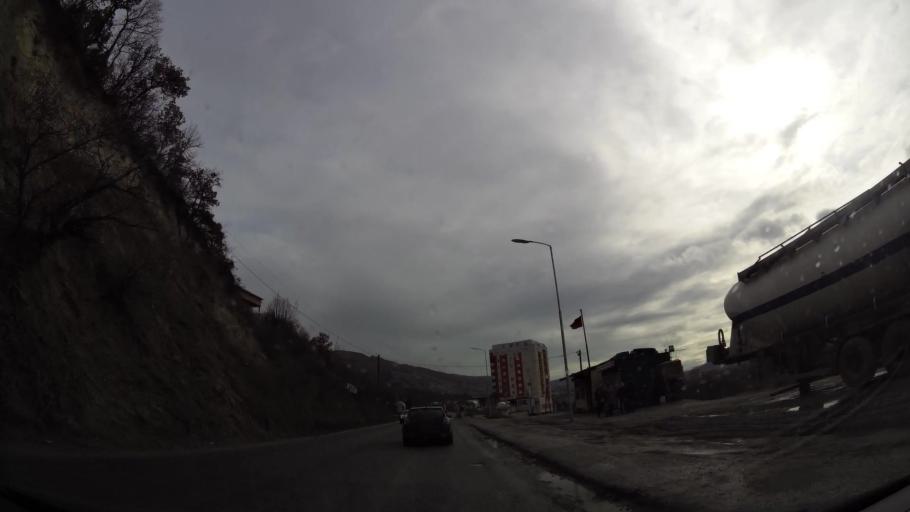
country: XK
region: Ferizaj
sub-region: Hani i Elezit
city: Hani i Elezit
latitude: 42.1567
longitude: 21.2927
